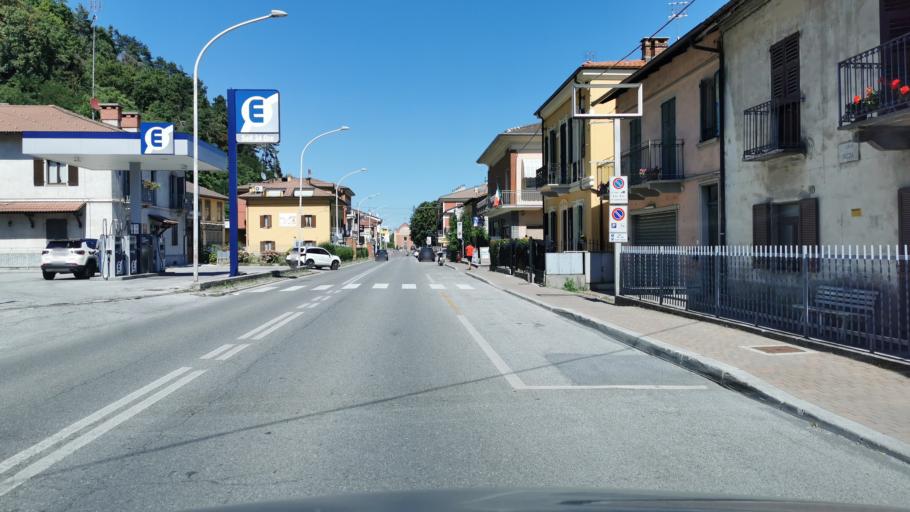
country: IT
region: Piedmont
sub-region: Provincia di Cuneo
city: Roccavione
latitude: 44.3255
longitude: 7.4837
